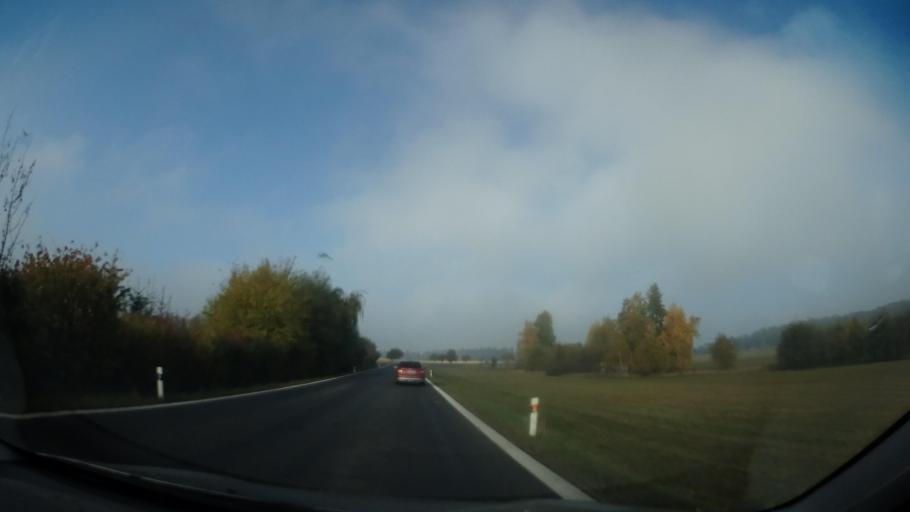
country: CZ
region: Vysocina
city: Krizanov
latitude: 49.4452
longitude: 16.1415
